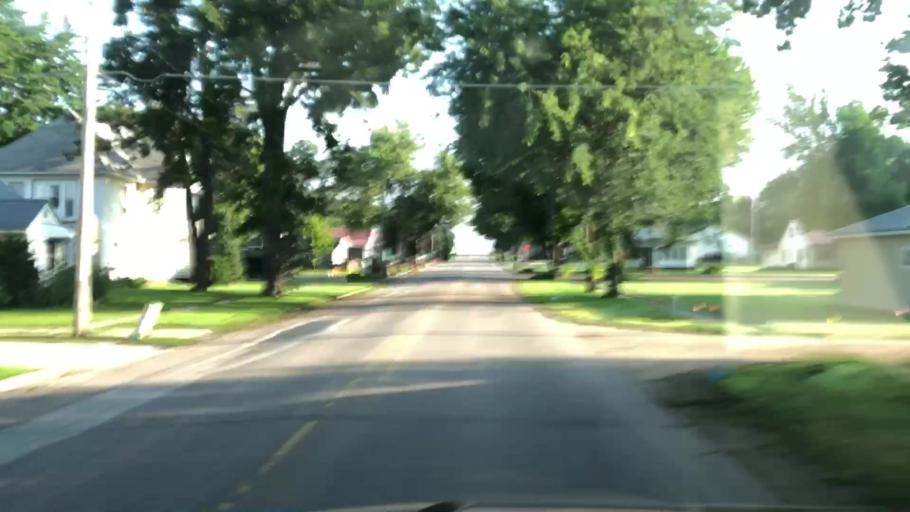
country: US
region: Iowa
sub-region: Lyon County
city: George
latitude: 43.3418
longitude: -95.9984
